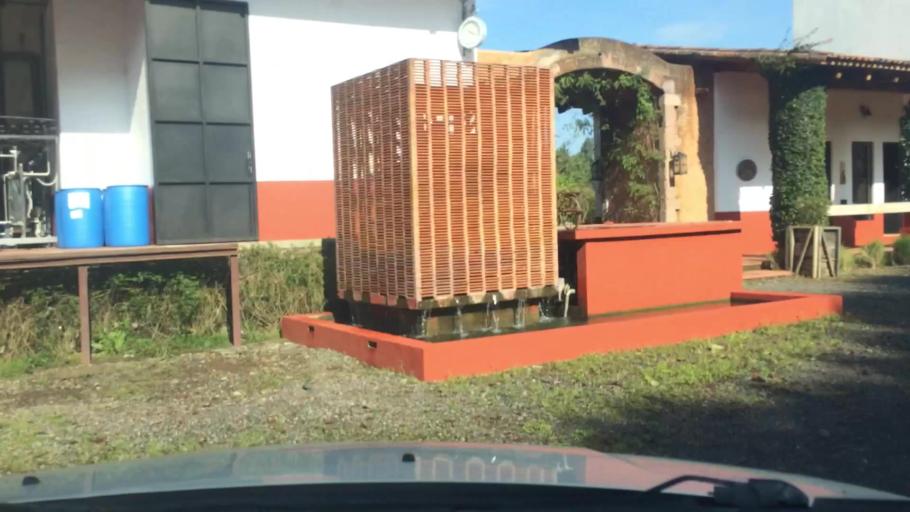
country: MX
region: Mexico
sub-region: Valle de Bravo
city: Cuadrilla de Dolores
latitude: 19.1533
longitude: -100.0587
